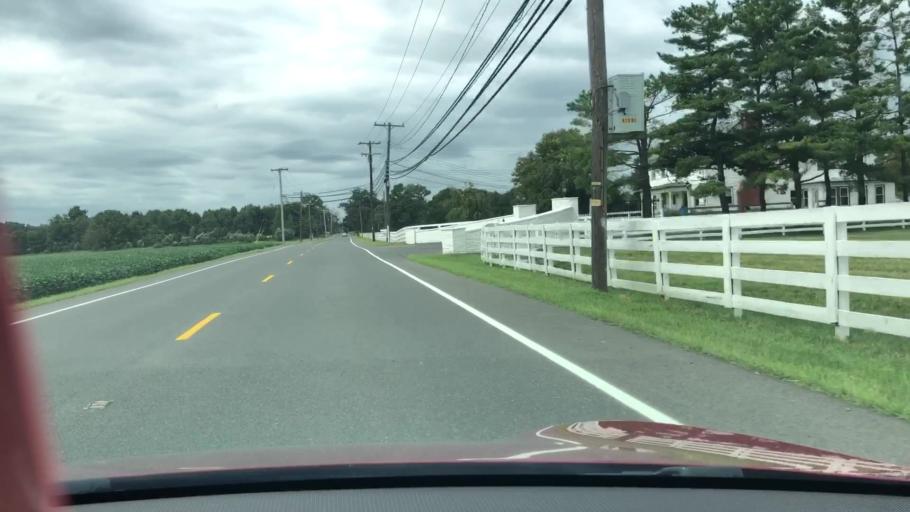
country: US
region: New Jersey
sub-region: Monmouth County
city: Shrewsbury
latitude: 40.1693
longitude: -74.5281
